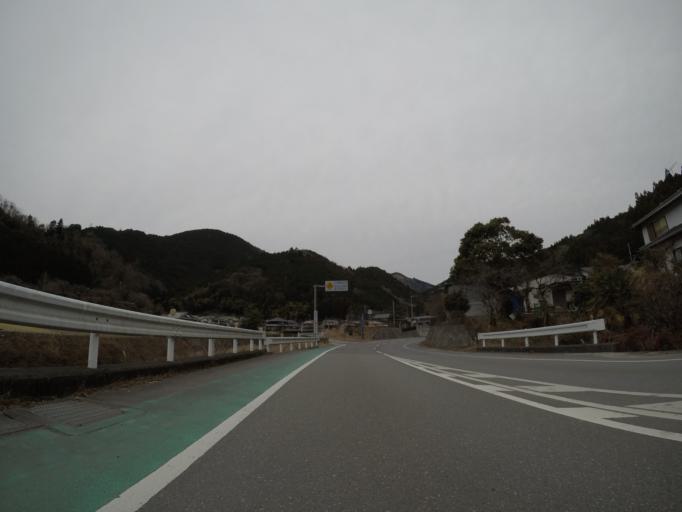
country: JP
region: Shizuoka
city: Fujinomiya
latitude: 35.2307
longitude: 138.5361
